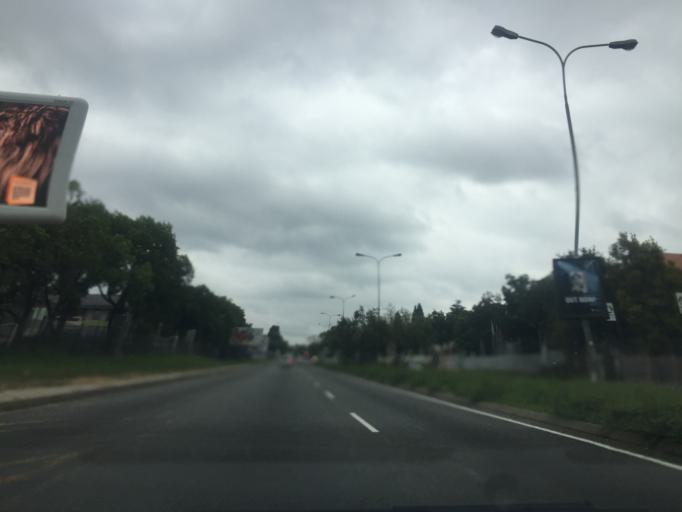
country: ZA
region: Gauteng
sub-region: City of Johannesburg Metropolitan Municipality
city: Midrand
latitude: -26.0415
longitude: 28.0604
